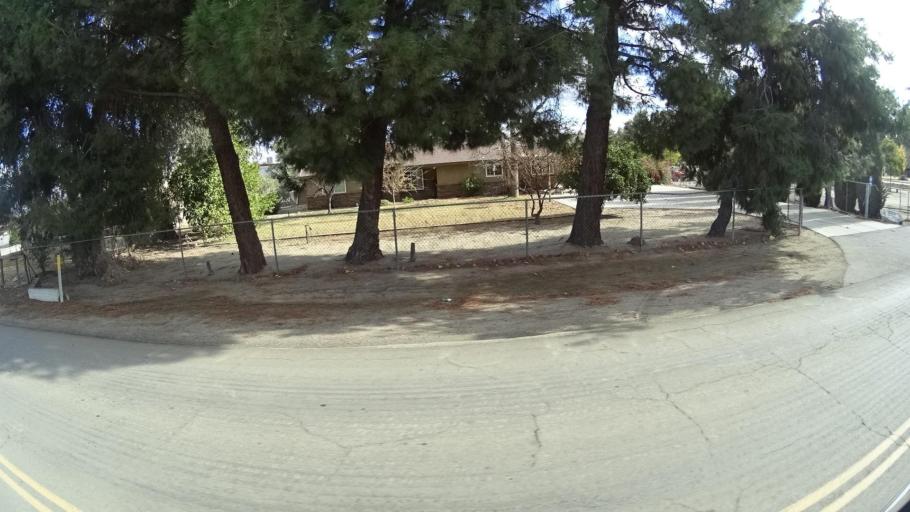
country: US
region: California
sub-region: Kern County
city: Greenfield
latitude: 35.2373
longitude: -119.0922
